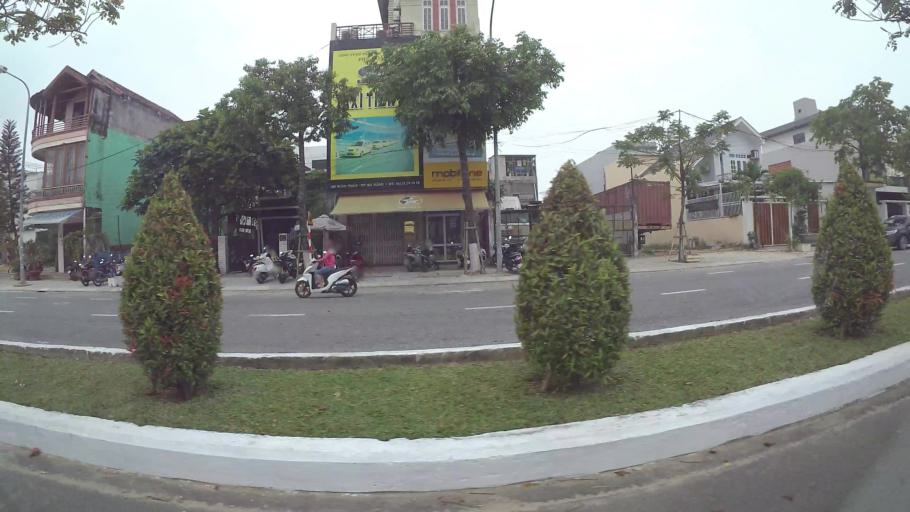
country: VN
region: Da Nang
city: Cam Le
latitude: 16.0256
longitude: 108.2151
